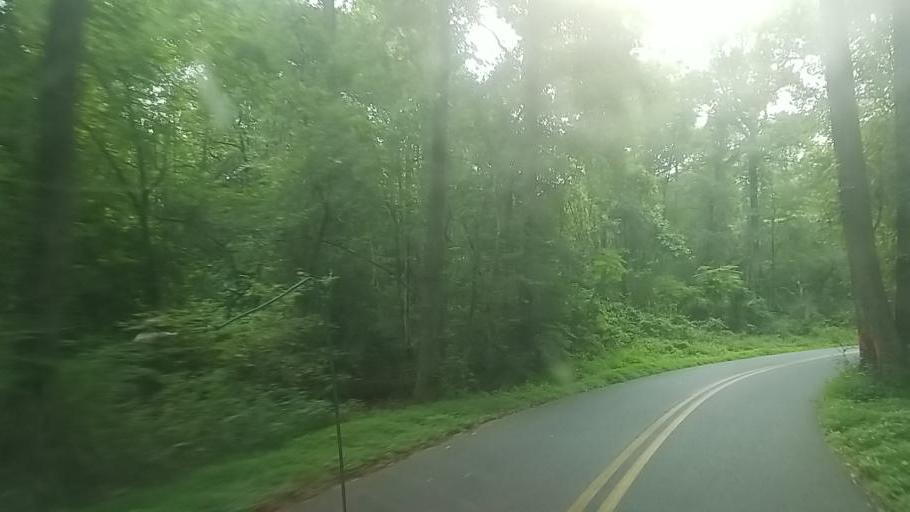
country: US
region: Maryland
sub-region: Wicomico County
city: Pittsville
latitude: 38.4405
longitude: -75.3323
